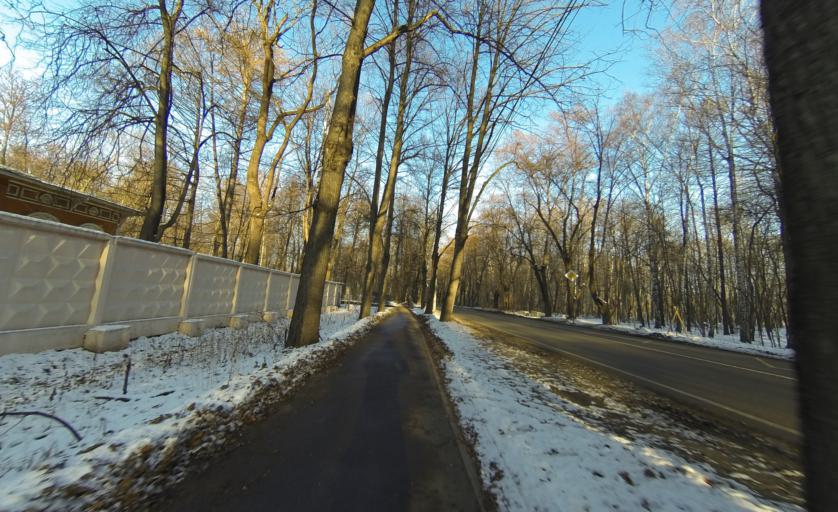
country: RU
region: Moscow
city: Sokol'niki
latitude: 55.8108
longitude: 37.6829
